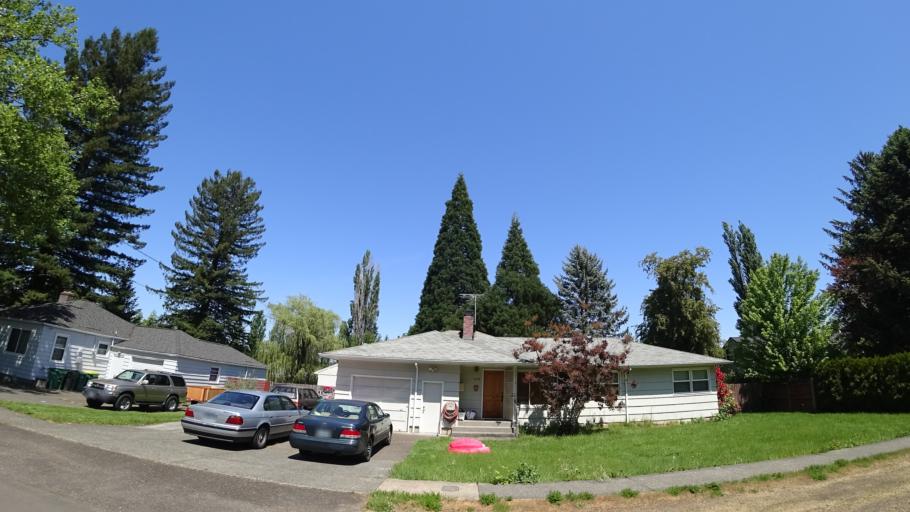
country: US
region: Oregon
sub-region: Washington County
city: Beaverton
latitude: 45.4858
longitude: -122.8161
